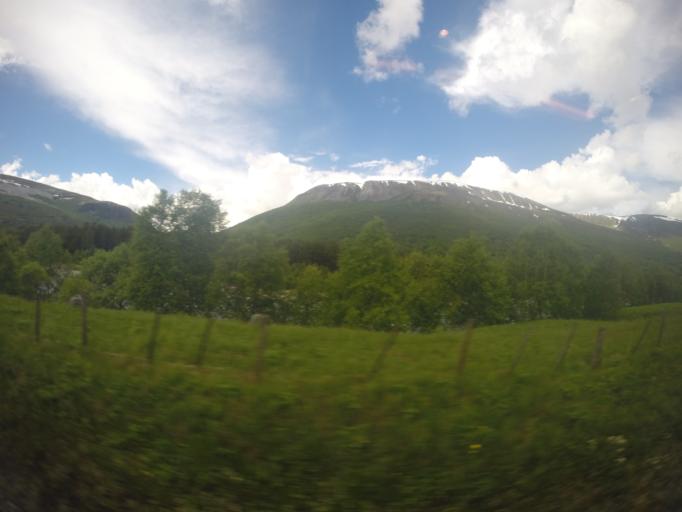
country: NO
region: Sor-Trondelag
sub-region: Oppdal
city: Oppdal
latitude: 62.5040
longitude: 9.5954
